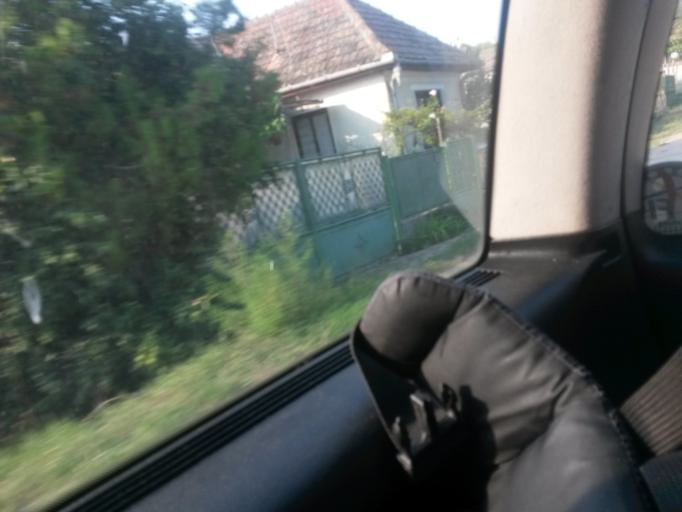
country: RO
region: Alba
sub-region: Municipiul Aiud
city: Aiudul de Sus
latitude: 46.3238
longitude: 23.6813
